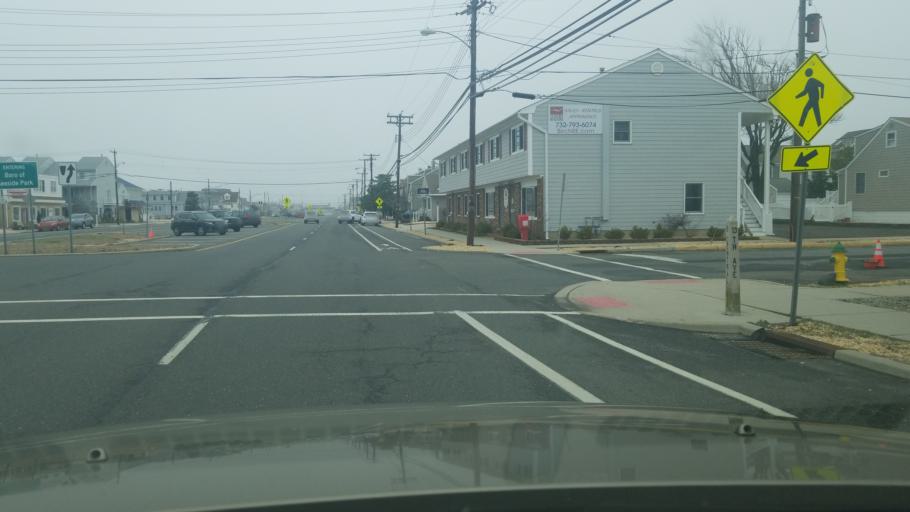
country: US
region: New Jersey
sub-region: Ocean County
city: Seaside Park
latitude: 39.9136
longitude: -74.0799
